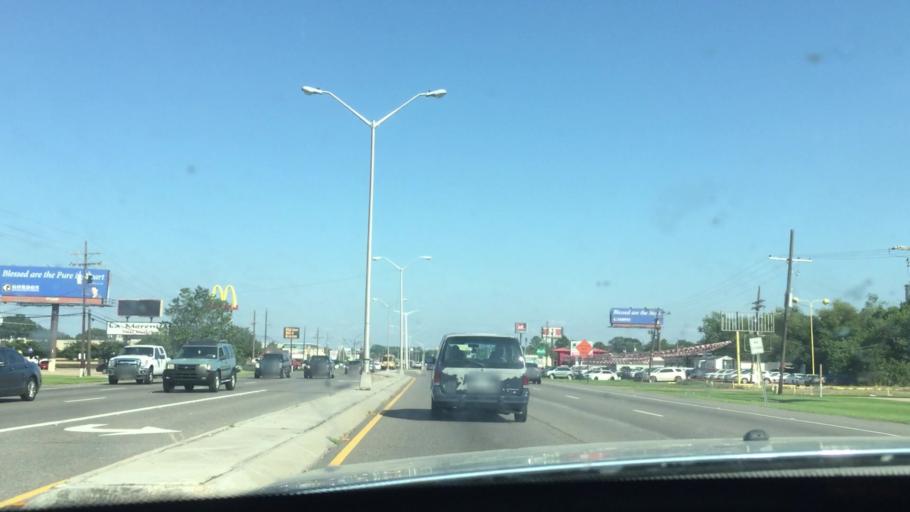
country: US
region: Louisiana
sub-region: East Baton Rouge Parish
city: Westminster
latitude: 30.4518
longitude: -91.1073
